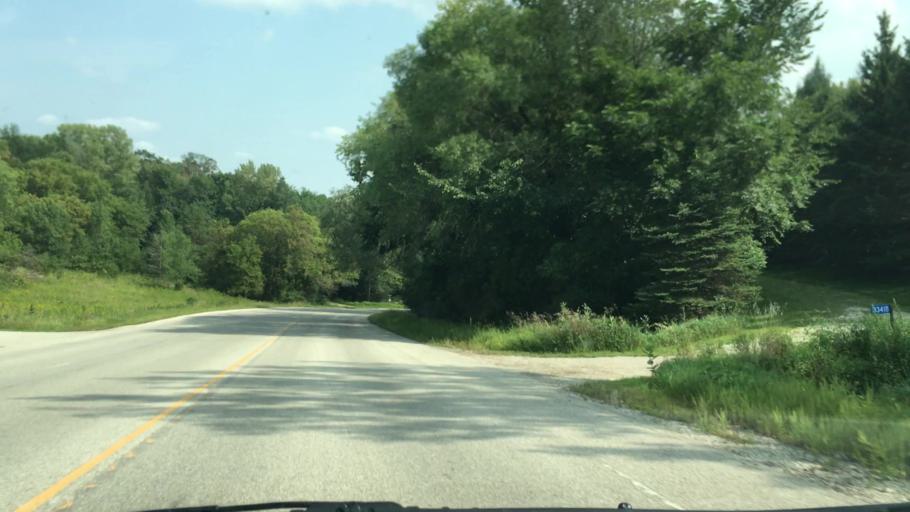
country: US
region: Minnesota
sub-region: Fillmore County
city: Preston
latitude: 43.7269
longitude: -91.9818
